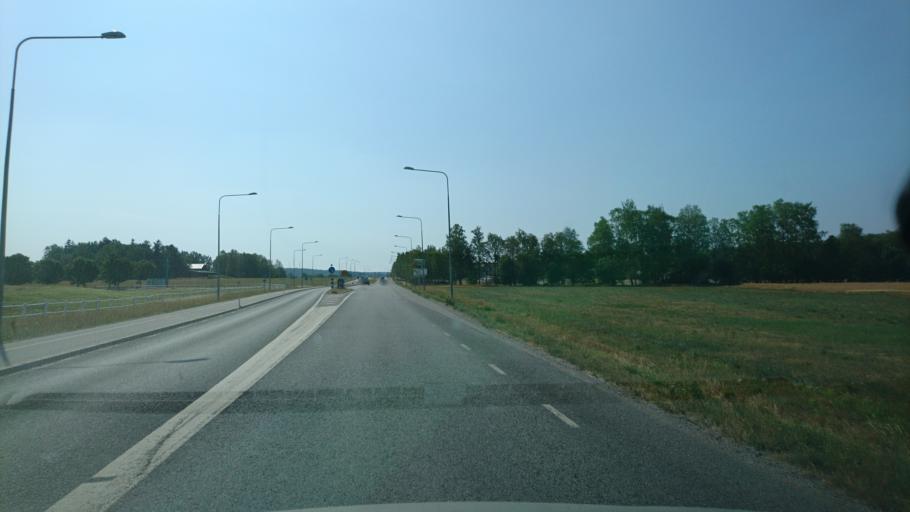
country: SE
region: Uppsala
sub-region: Uppsala Kommun
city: Uppsala
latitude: 59.8196
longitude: 17.6473
